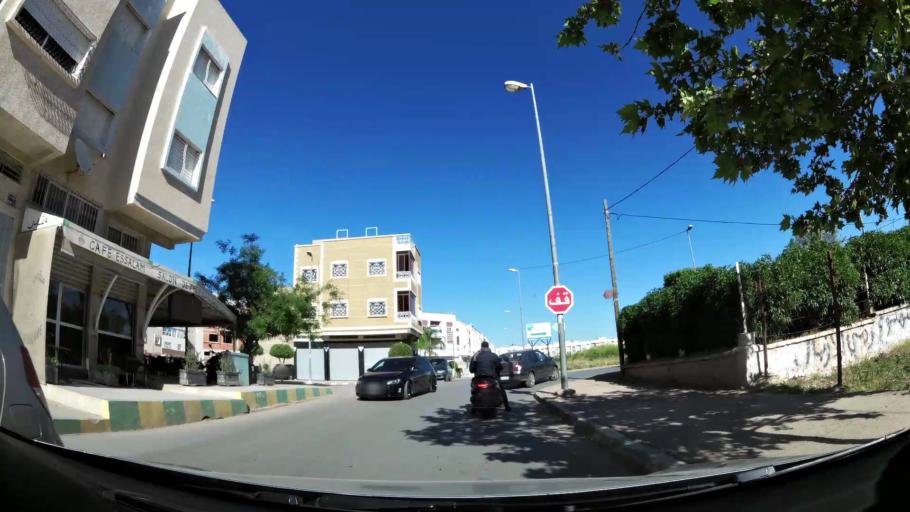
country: MA
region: Fes-Boulemane
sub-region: Fes
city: Fes
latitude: 34.0100
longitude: -5.0161
